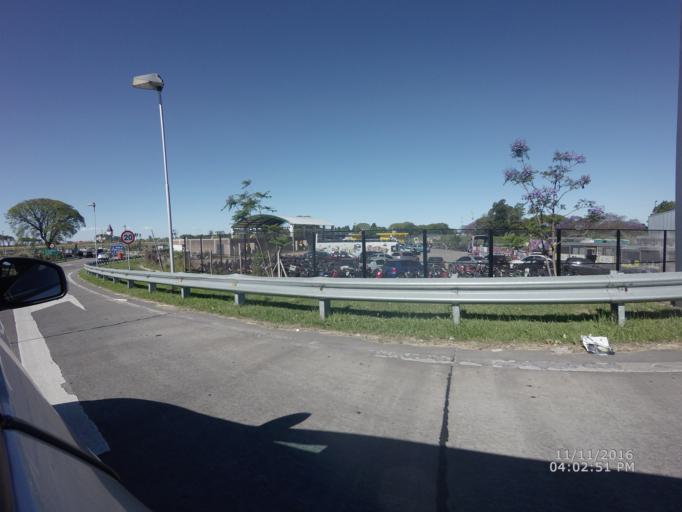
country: AR
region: Buenos Aires F.D.
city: Retiro
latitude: -34.5678
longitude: -58.4056
